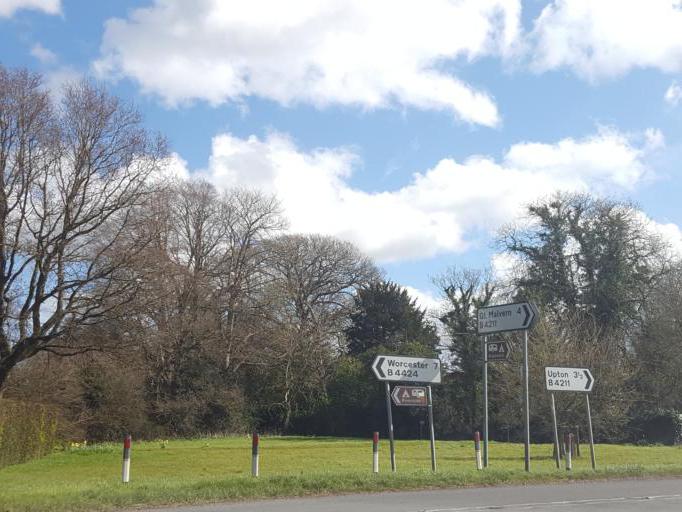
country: GB
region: England
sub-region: Worcestershire
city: Kempsey
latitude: 52.1041
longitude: -2.2423
